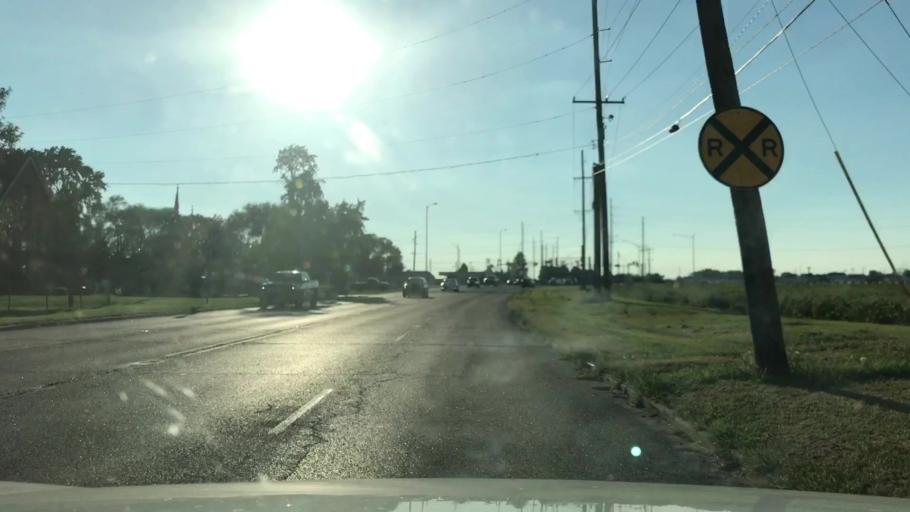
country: US
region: Illinois
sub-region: Madison County
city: Granite City
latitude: 38.7315
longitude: -90.1341
